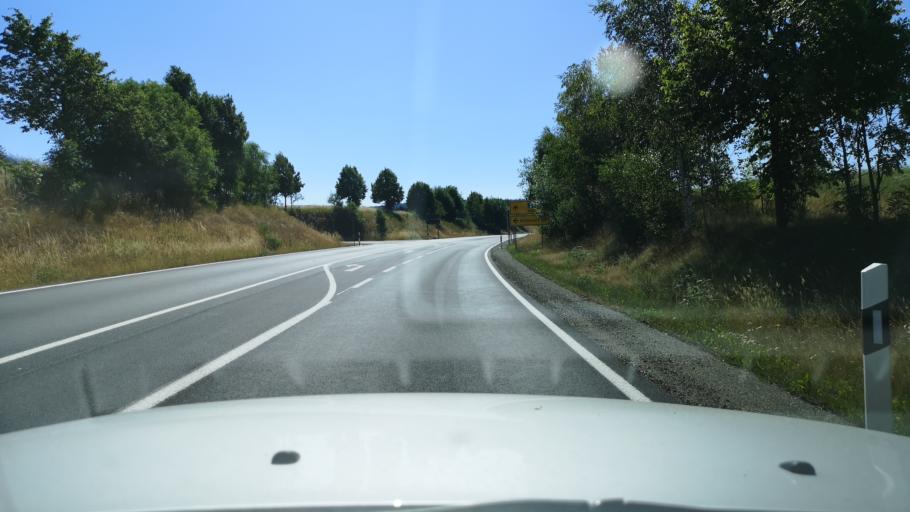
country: DE
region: Thuringia
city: Birkenhugel
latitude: 50.4465
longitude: 11.7901
